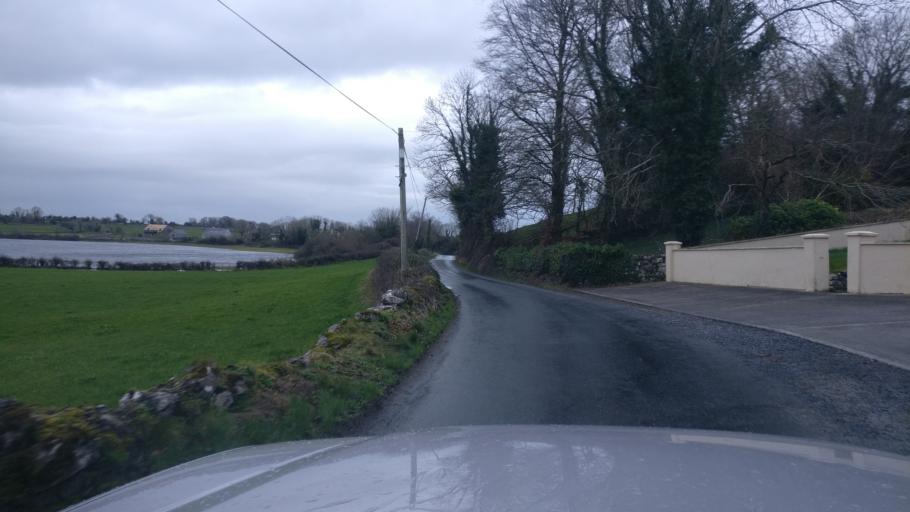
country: IE
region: Connaught
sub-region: County Galway
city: Athenry
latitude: 53.1855
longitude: -8.7079
